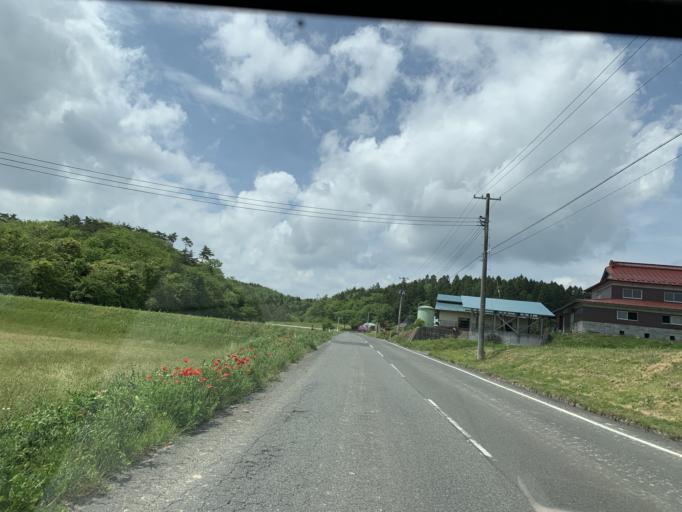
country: JP
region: Miyagi
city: Furukawa
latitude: 38.7662
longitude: 140.9442
